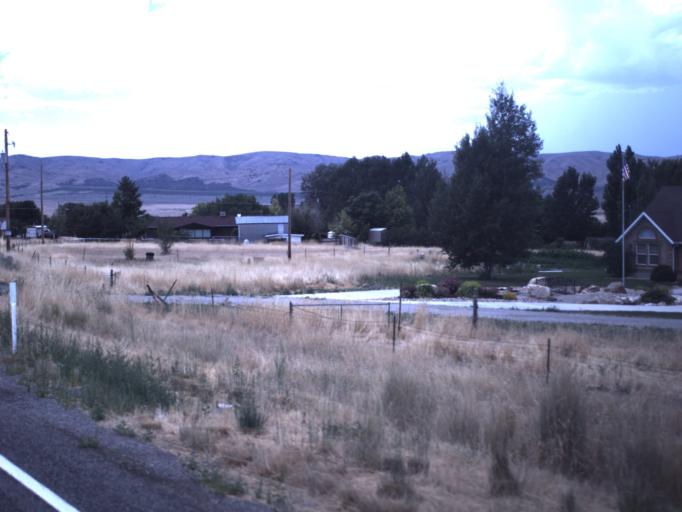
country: US
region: Utah
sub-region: Juab County
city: Mona
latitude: 39.8196
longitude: -111.8489
